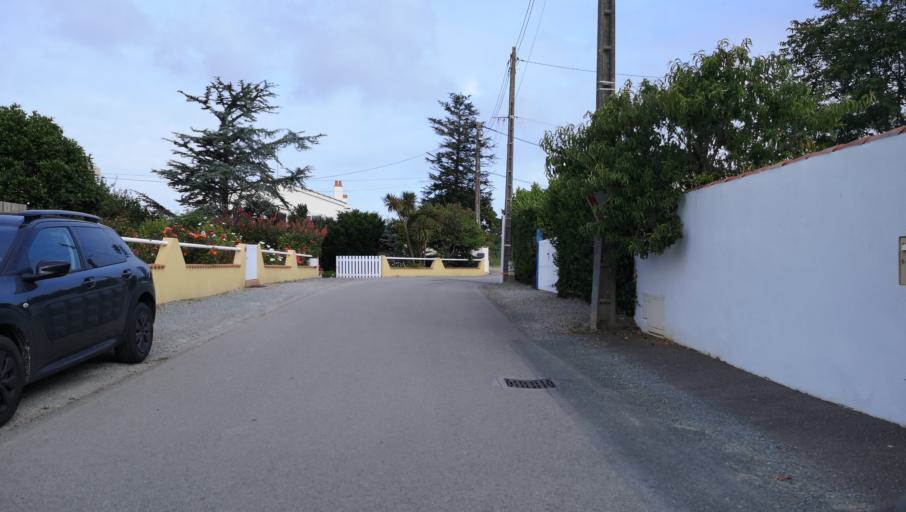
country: FR
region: Pays de la Loire
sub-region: Departement de la Vendee
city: Olonne-sur-Mer
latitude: 46.5433
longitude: -1.8023
